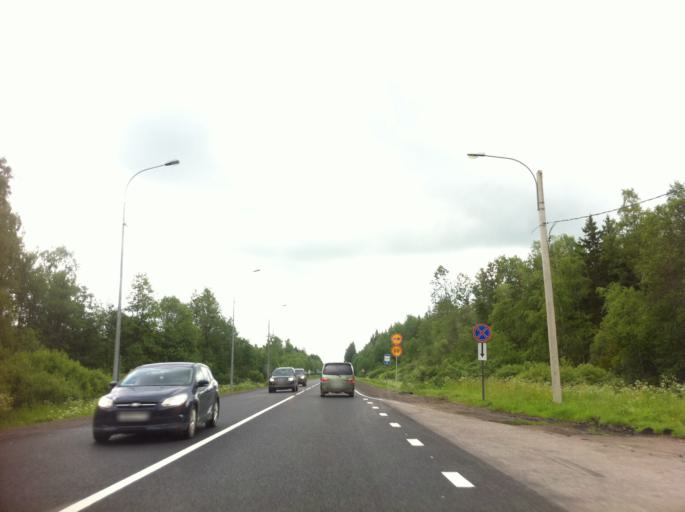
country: RU
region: Leningrad
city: Rozhdestveno
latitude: 59.1964
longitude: 29.9213
